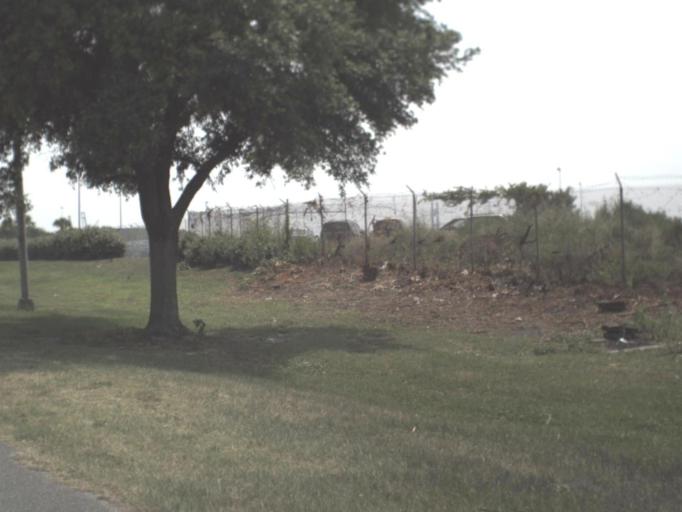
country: US
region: Florida
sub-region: Duval County
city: Jacksonville
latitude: 30.4063
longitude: -81.5368
